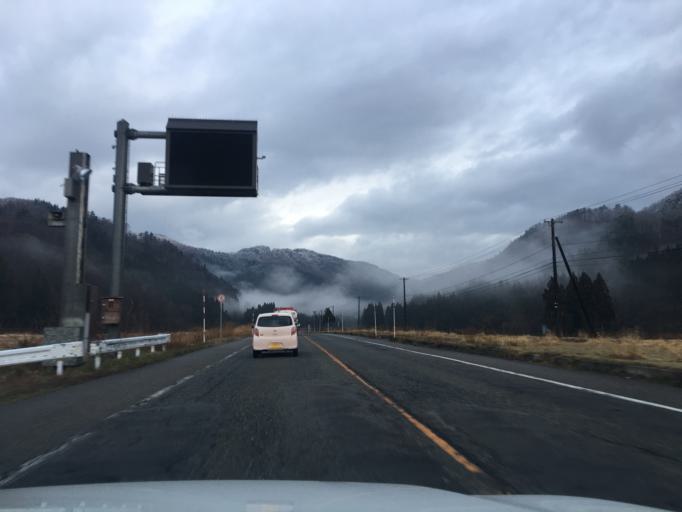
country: JP
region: Niigata
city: Murakami
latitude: 38.4436
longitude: 139.5856
